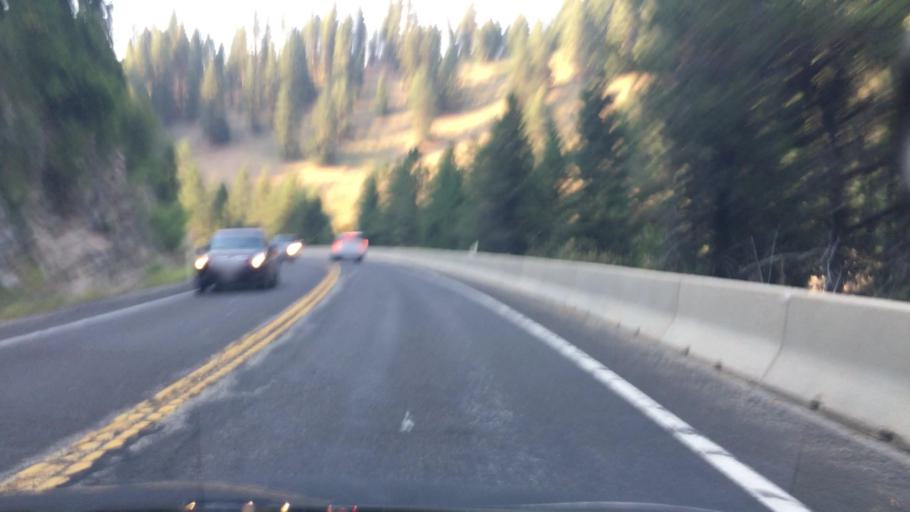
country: US
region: Idaho
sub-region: Valley County
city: Cascade
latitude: 44.2635
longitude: -116.0671
